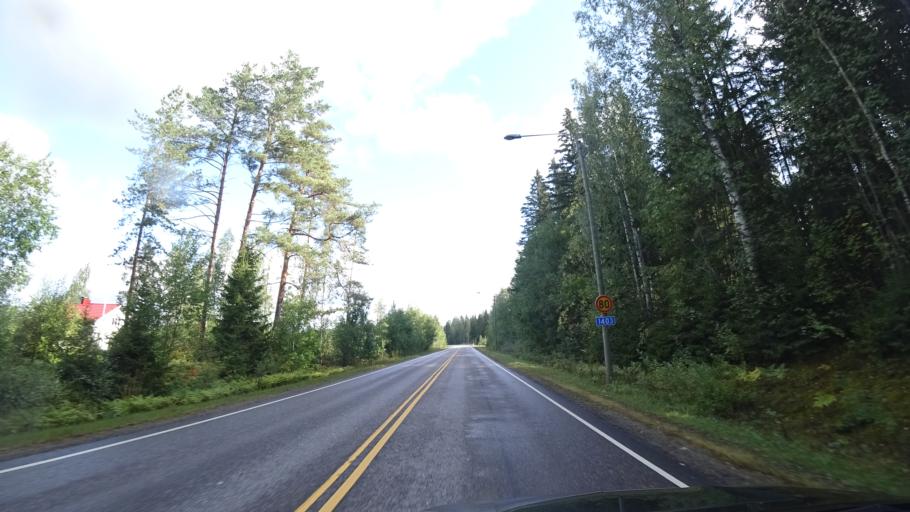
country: FI
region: Uusimaa
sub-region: Helsinki
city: Hyvinge
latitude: 60.5341
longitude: 24.9199
